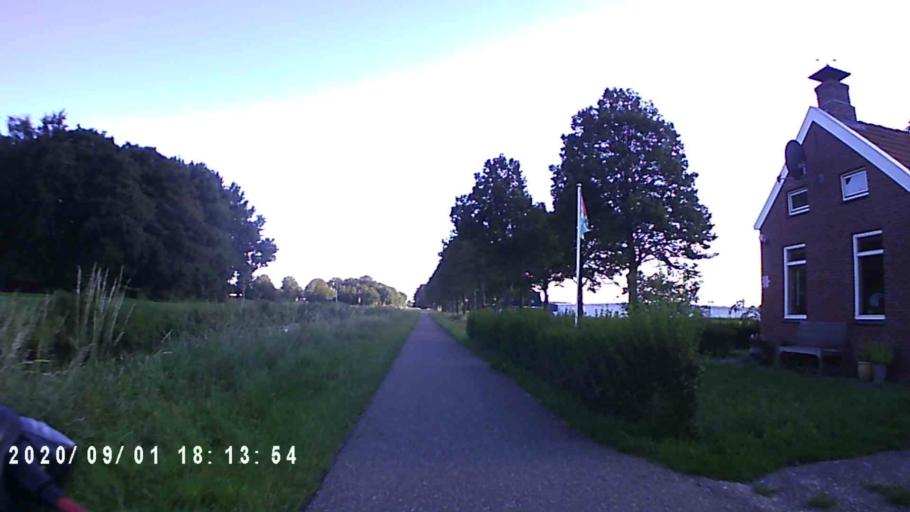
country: NL
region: Groningen
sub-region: Gemeente Hoogezand-Sappemeer
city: Sappemeer
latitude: 53.1818
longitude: 6.7863
